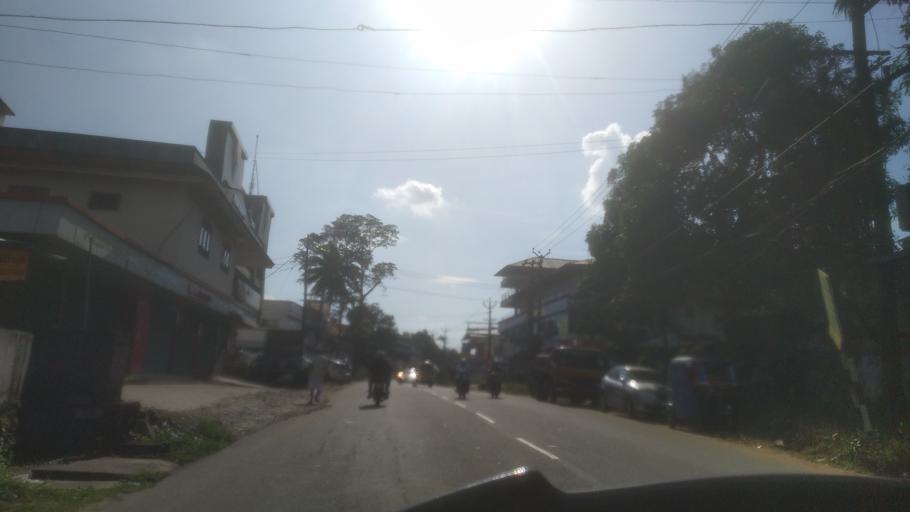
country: IN
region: Kerala
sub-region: Ernakulam
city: Muvattupula
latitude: 9.9905
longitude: 76.5739
